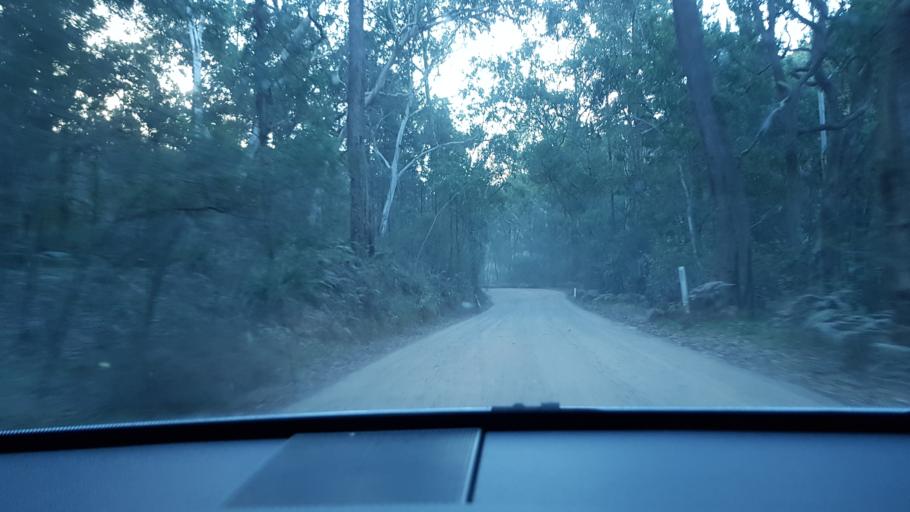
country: AU
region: New South Wales
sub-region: Lithgow
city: Portland
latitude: -33.1858
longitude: 150.2441
